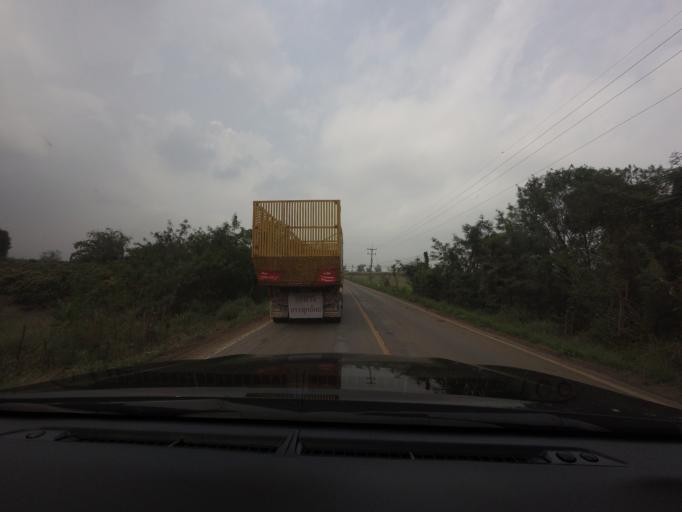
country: TH
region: Nakhon Ratchasima
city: Wang Nam Khiao
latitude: 14.4838
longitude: 101.6184
